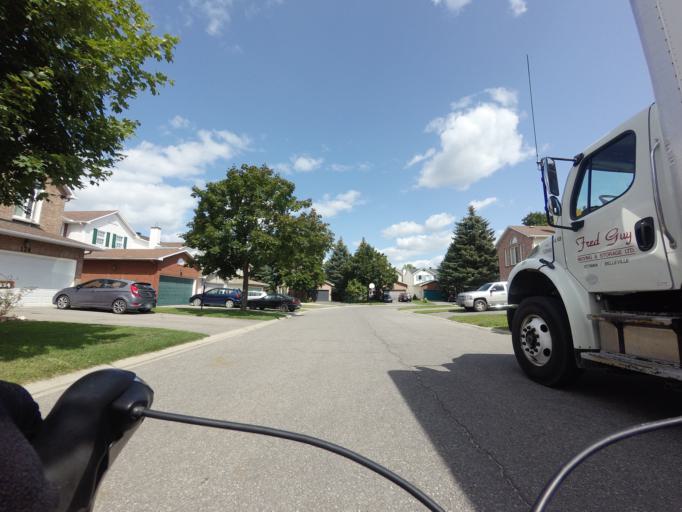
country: CA
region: Ontario
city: Bells Corners
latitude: 45.3026
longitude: -75.8576
